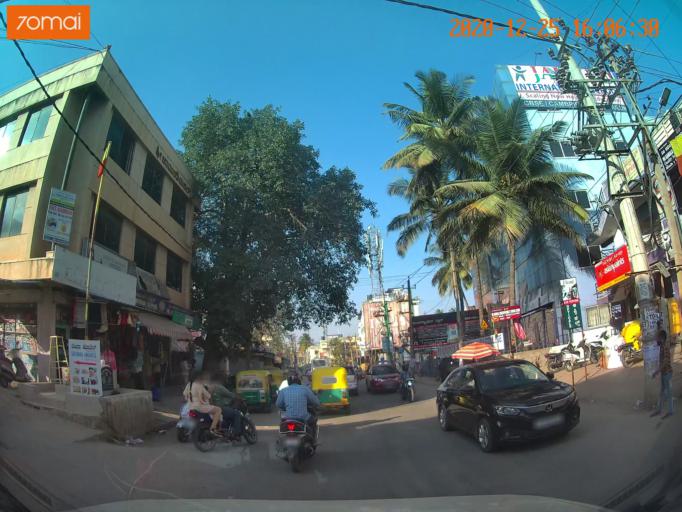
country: IN
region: Karnataka
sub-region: Bangalore Urban
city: Bangalore
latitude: 12.8921
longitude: 77.6259
